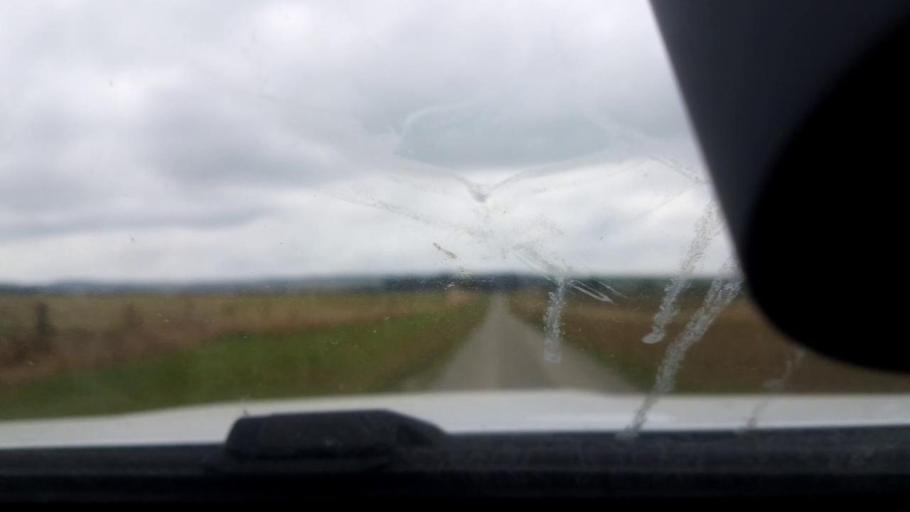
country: NZ
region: Canterbury
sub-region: Timaru District
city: Pleasant Point
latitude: -44.2296
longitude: 171.1660
